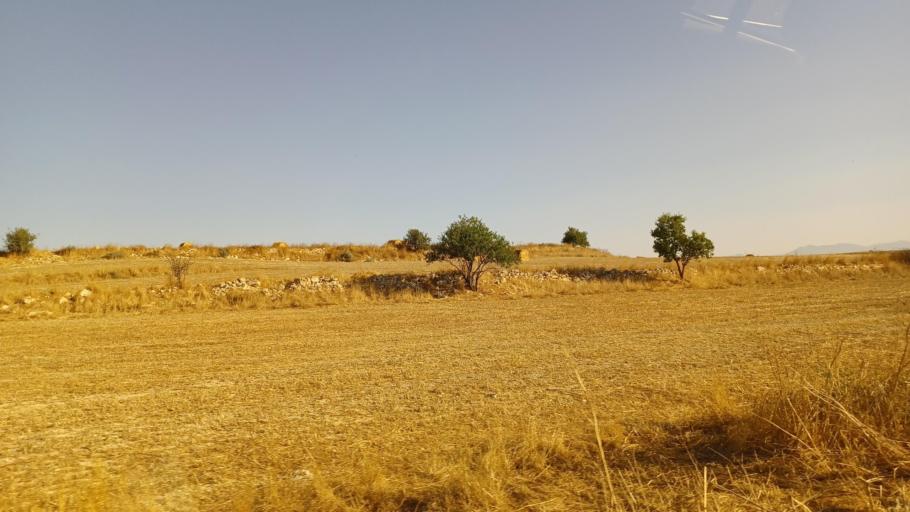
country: CY
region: Larnaka
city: Athienou
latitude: 35.0379
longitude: 33.5300
